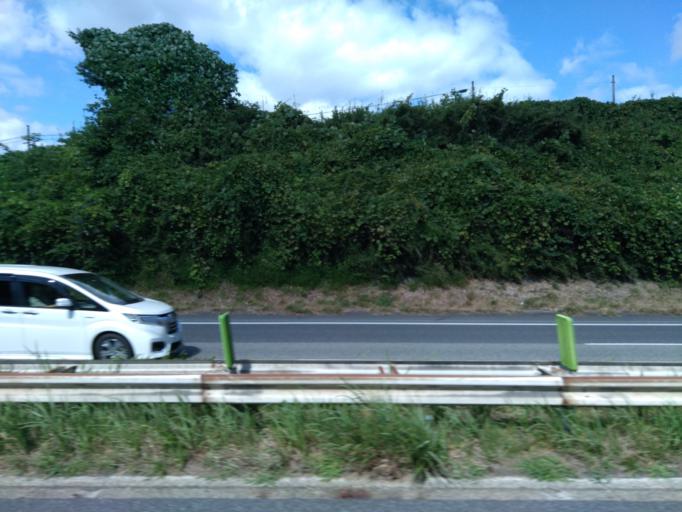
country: JP
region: Miyagi
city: Kogota
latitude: 38.7360
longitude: 141.0439
